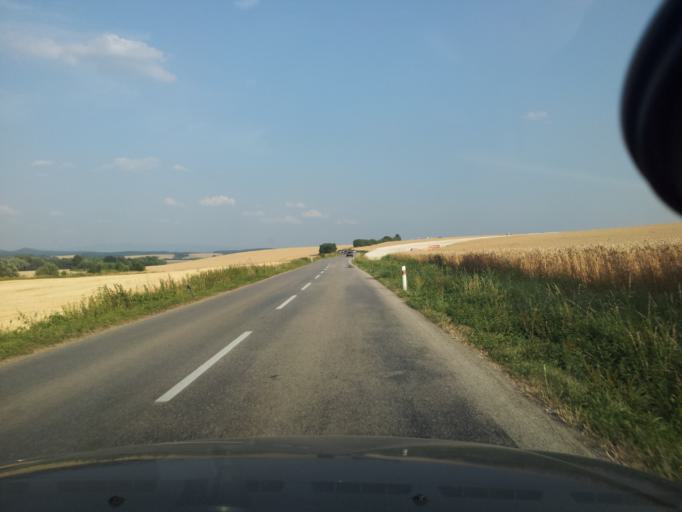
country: SK
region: Nitriansky
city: Banovce nad Bebravou
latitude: 48.7474
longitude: 18.2231
